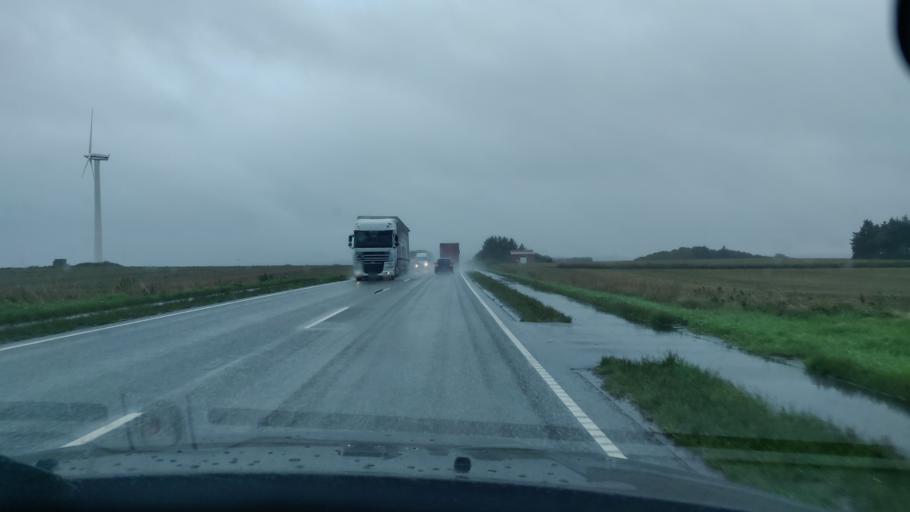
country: DK
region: North Denmark
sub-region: Thisted Kommune
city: Thisted
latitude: 56.8837
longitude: 8.5989
